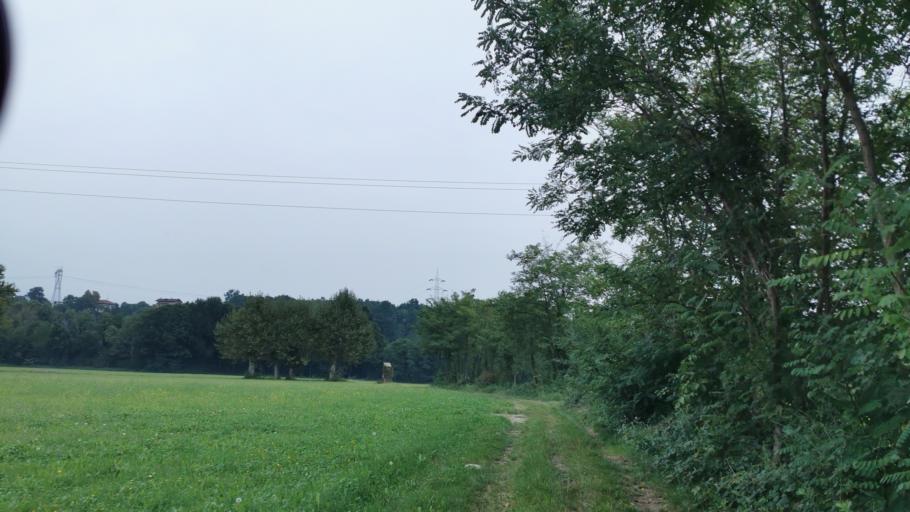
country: IT
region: Piedmont
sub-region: Provincia di Torino
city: Grosso
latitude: 45.2627
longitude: 7.5498
